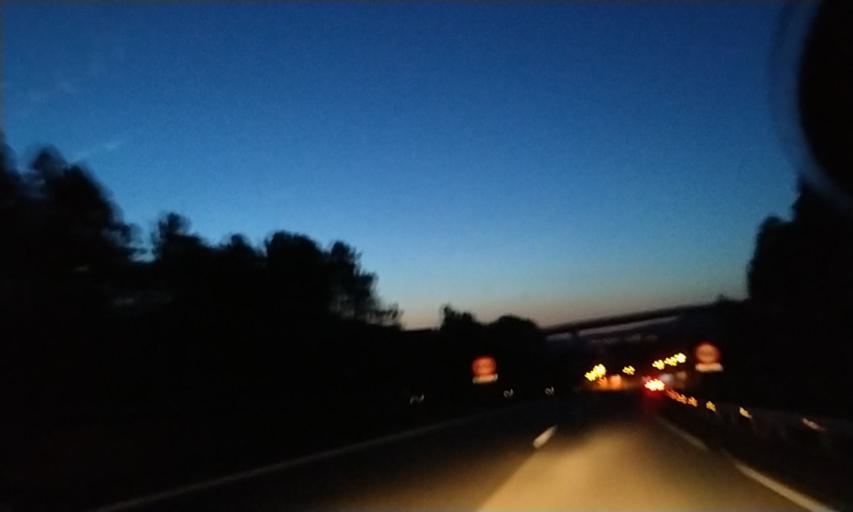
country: ES
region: Galicia
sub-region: Provincia da Coruna
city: Ribeira
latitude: 42.7491
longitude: -8.3890
